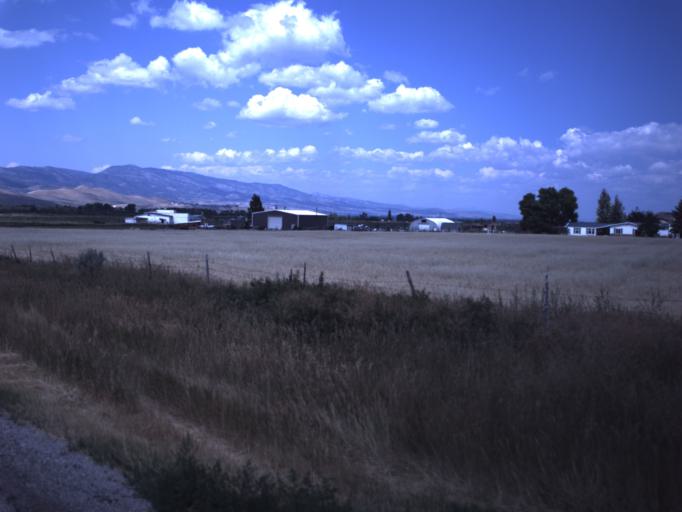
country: US
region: Utah
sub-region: Rich County
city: Randolph
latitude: 41.8294
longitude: -111.3173
